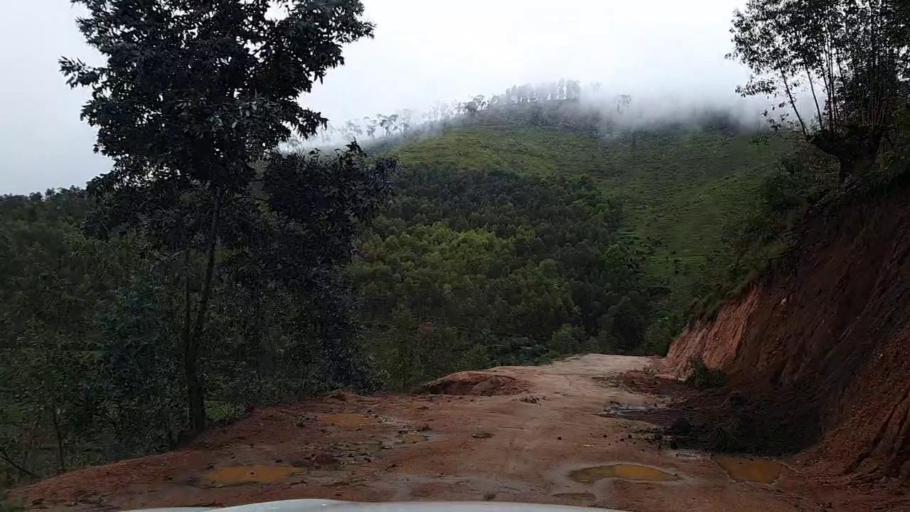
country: RW
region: Southern Province
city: Nzega
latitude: -2.3938
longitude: 29.4982
